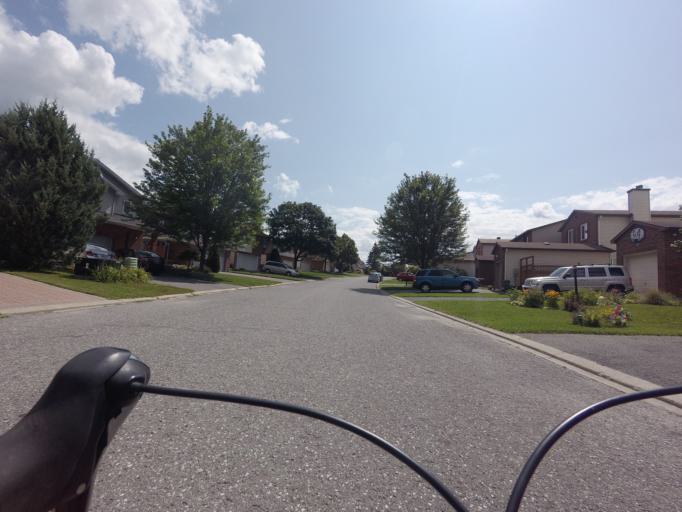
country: CA
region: Ontario
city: Bells Corners
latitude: 45.2879
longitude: -75.8628
